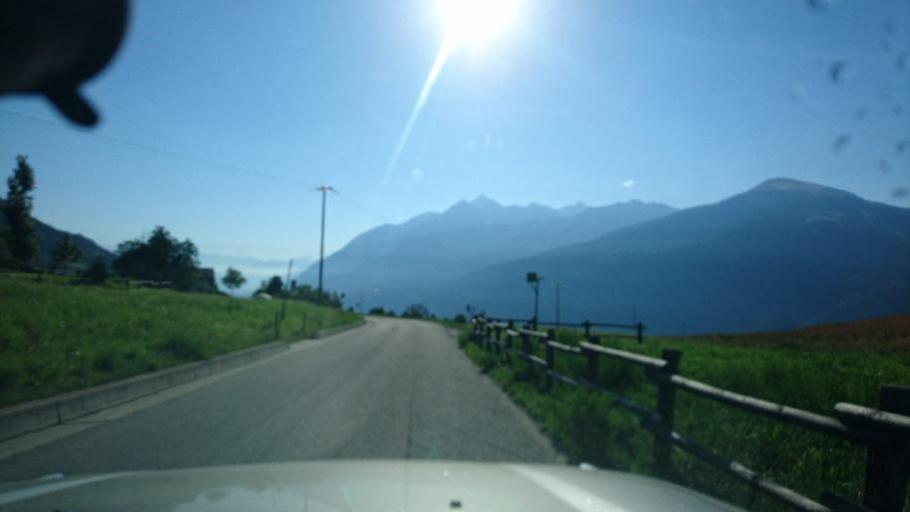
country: IT
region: Aosta Valley
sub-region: Valle d'Aosta
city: Villeneuve
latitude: 45.7189
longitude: 7.2043
